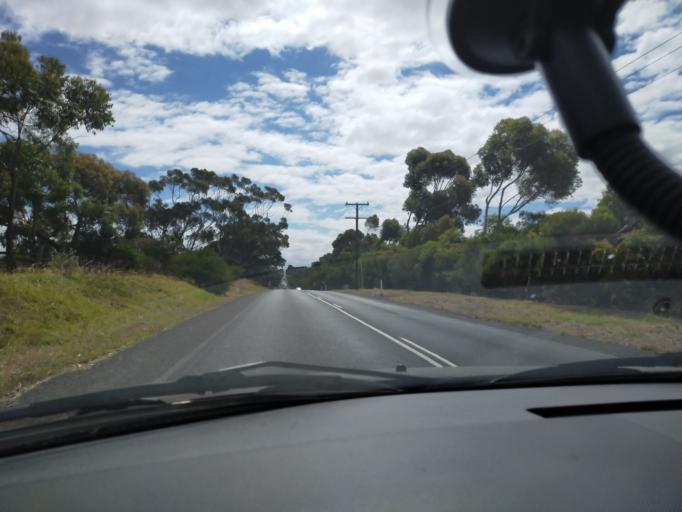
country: AU
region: Victoria
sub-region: Greater Geelong
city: Breakwater
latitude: -38.2500
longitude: 144.3455
